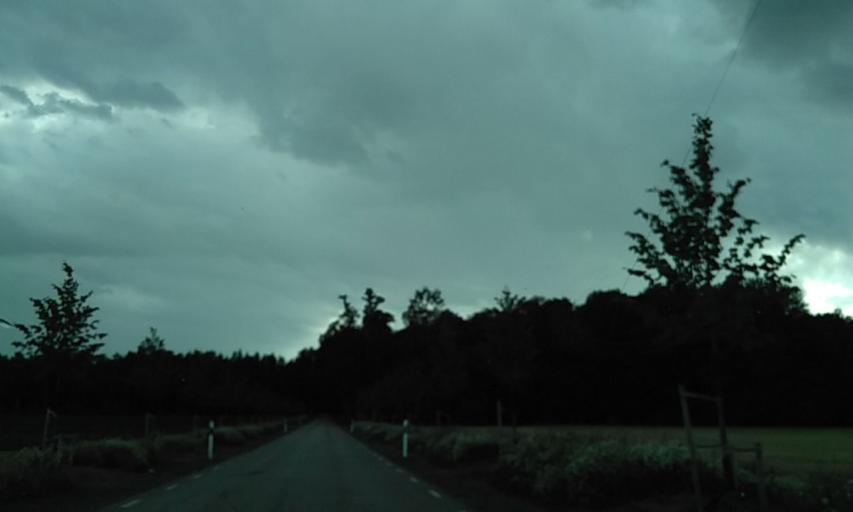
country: SE
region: Vaestra Goetaland
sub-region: Grastorps Kommun
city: Graestorp
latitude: 58.4680
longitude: 12.8125
